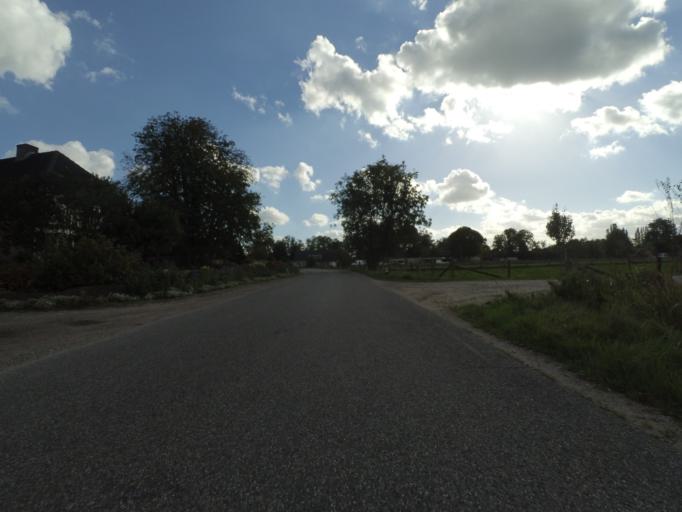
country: NL
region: Gelderland
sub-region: Gemeente Ede
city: Ederveen
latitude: 52.0513
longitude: 5.5962
